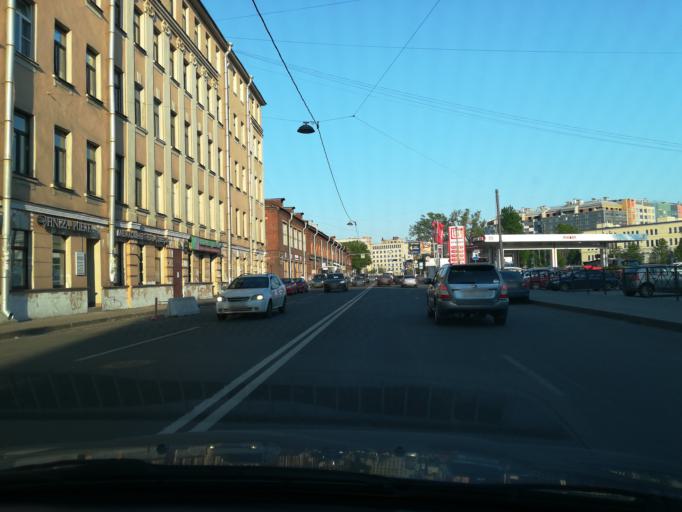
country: RU
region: St.-Petersburg
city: Vasyl'evsky Ostrov
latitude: 59.9535
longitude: 30.2603
